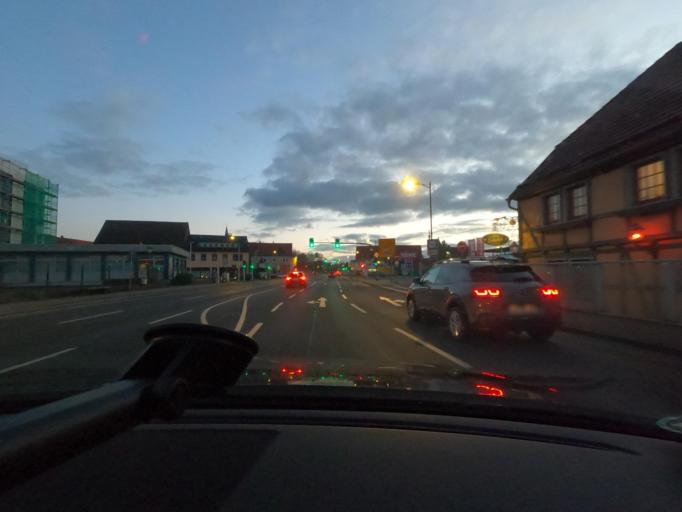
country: DE
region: Lower Saxony
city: Herzberg am Harz
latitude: 51.6564
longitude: 10.3340
